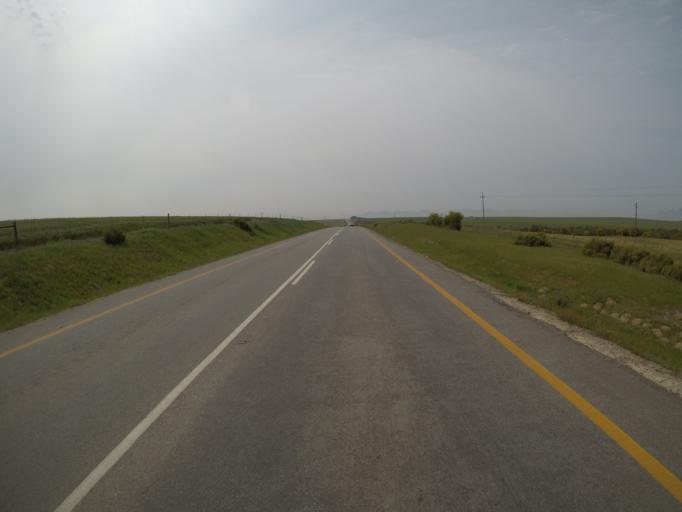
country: ZA
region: Western Cape
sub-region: City of Cape Town
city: Kraaifontein
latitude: -33.6964
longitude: 18.7111
